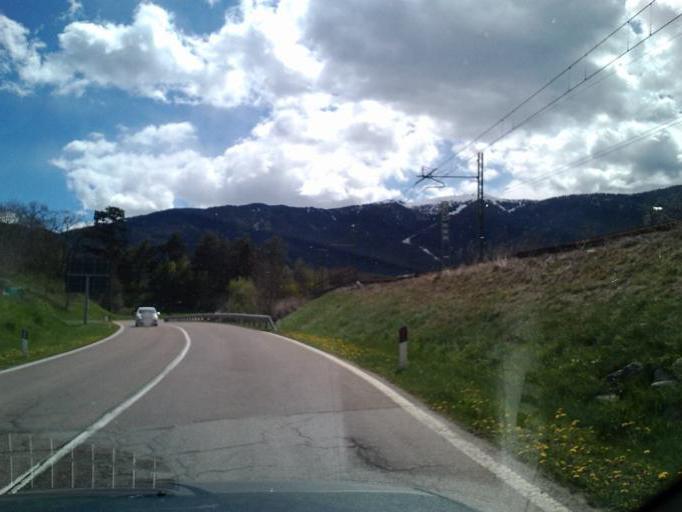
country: IT
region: Trentino-Alto Adige
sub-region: Bolzano
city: Brunico
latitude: 46.7965
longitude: 11.9505
